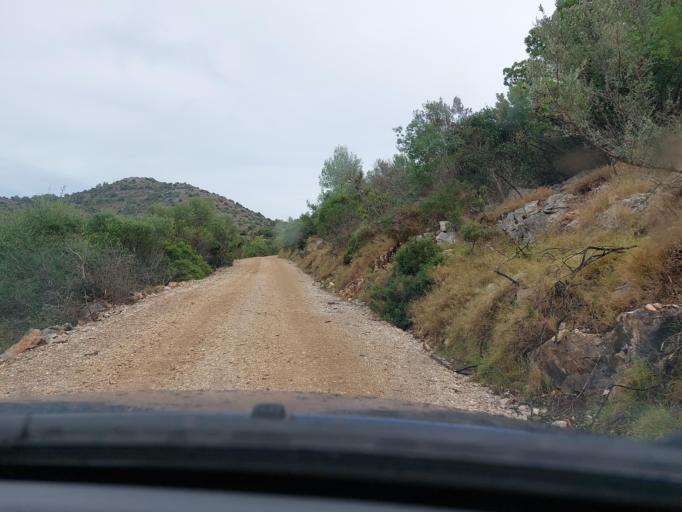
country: HR
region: Dubrovacko-Neretvanska
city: Smokvica
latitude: 42.7384
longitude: 16.9078
